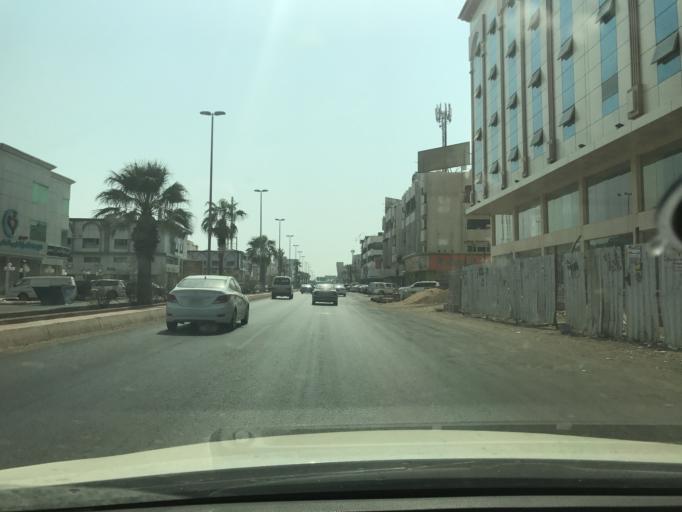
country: SA
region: Makkah
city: Jeddah
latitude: 21.6155
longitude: 39.1633
